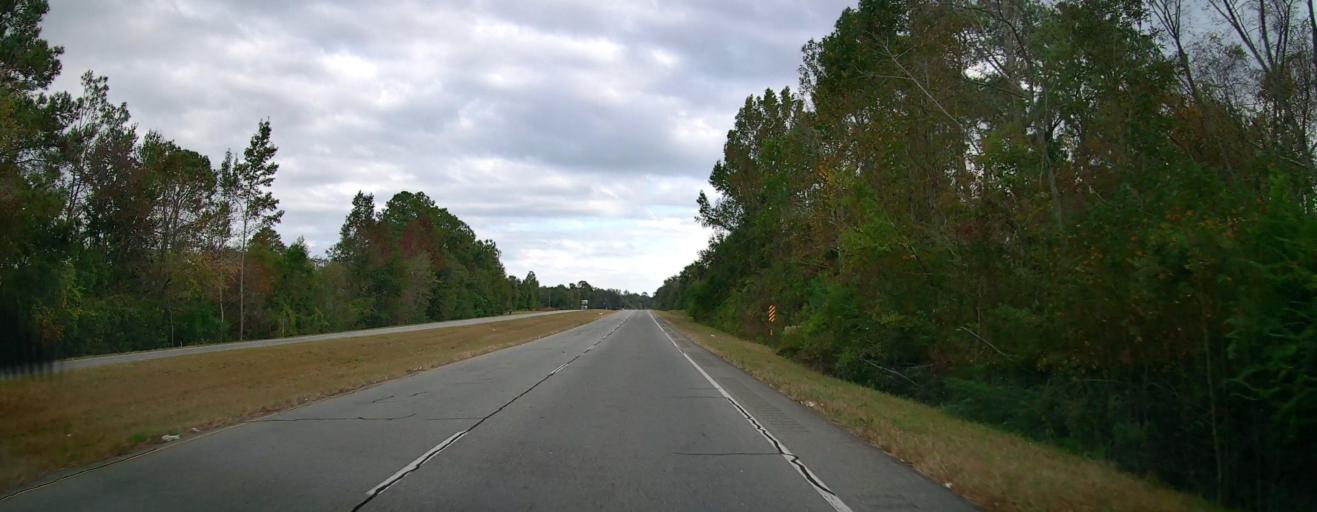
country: US
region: Georgia
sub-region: Thomas County
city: Meigs
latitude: 31.0844
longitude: -84.0862
